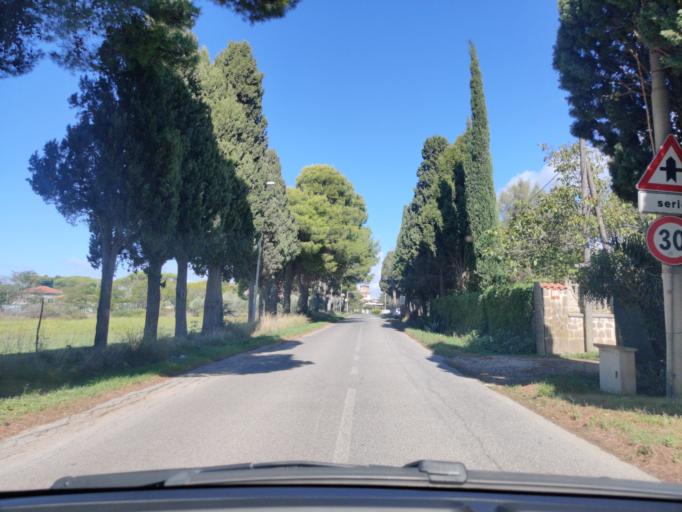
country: IT
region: Latium
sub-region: Citta metropolitana di Roma Capitale
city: Aurelia
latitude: 42.1353
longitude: 11.7883
